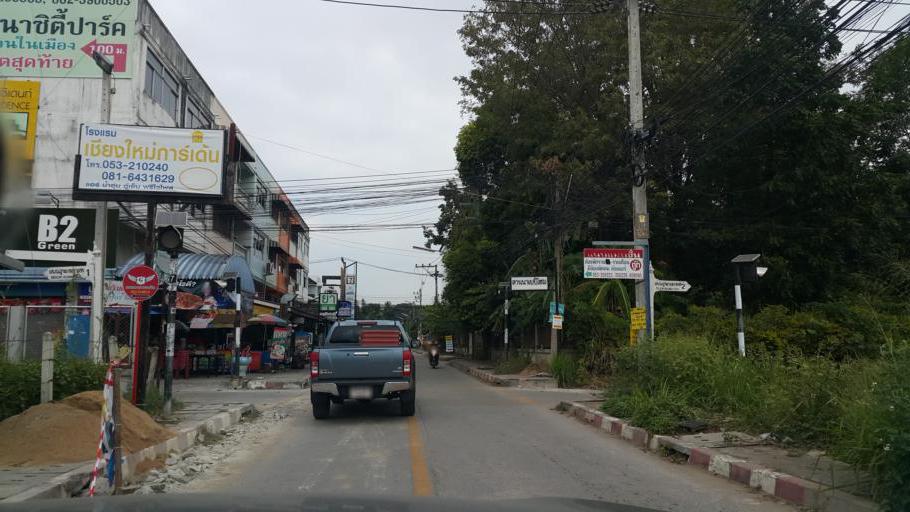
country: TH
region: Chiang Mai
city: Chiang Mai
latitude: 18.8162
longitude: 98.9920
